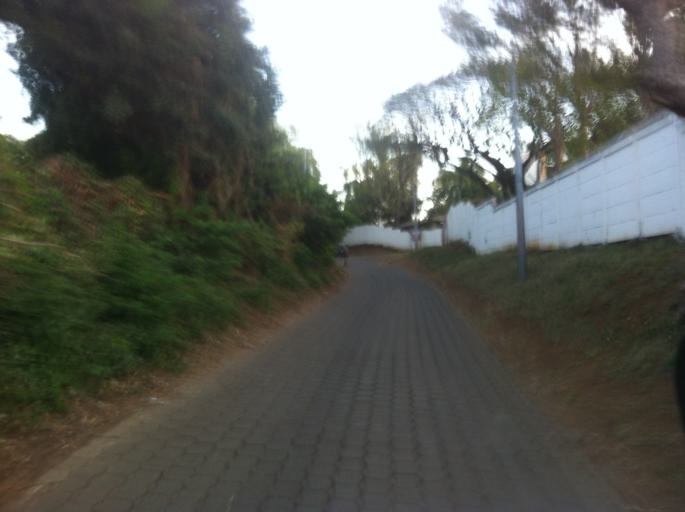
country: NI
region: Managua
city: Ciudad Sandino
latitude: 12.0818
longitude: -86.3336
